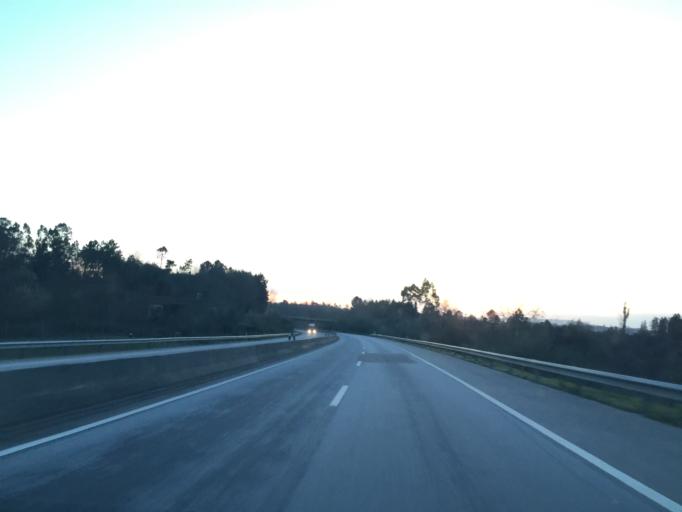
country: PT
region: Viseu
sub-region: Santa Comba Dao
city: Santa Comba Dao
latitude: 40.3981
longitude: -8.0933
